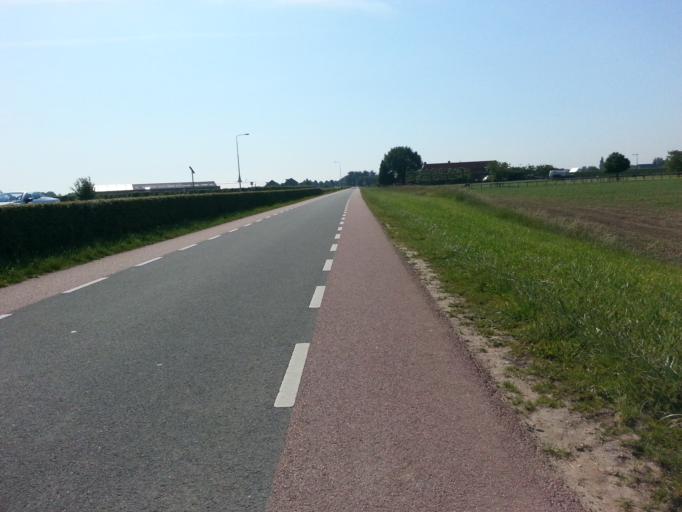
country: NL
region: Utrecht
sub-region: Gemeente Utrechtse Heuvelrug
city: Driebergen-Rijsenburg
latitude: 52.0037
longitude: 5.2950
